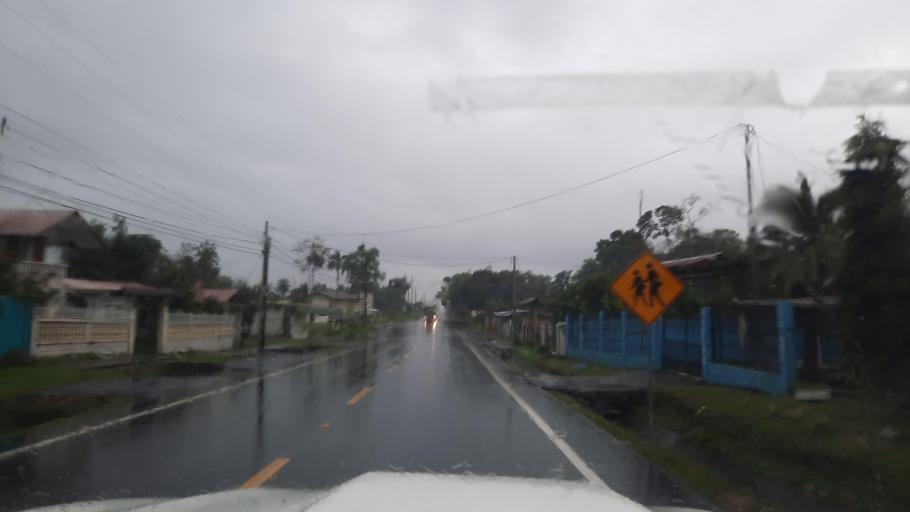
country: PA
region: Chiriqui
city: Sortova
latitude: 8.5867
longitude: -82.6370
